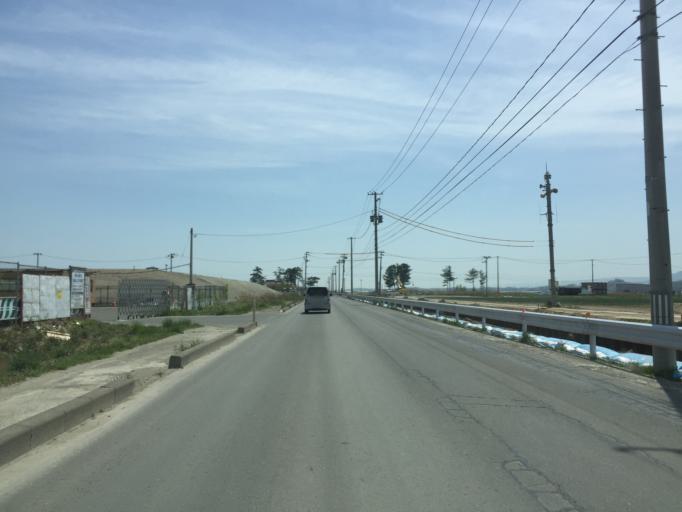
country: JP
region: Miyagi
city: Watari
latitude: 37.9604
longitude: 140.9090
